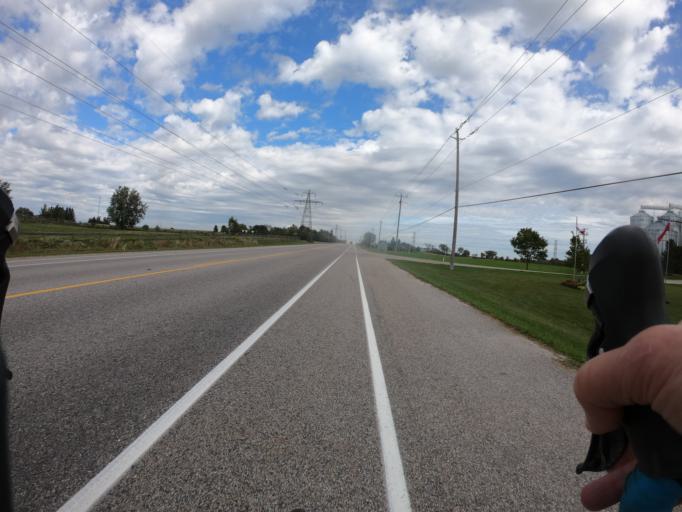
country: CA
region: Ontario
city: Waterloo
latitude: 43.4376
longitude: -80.6114
